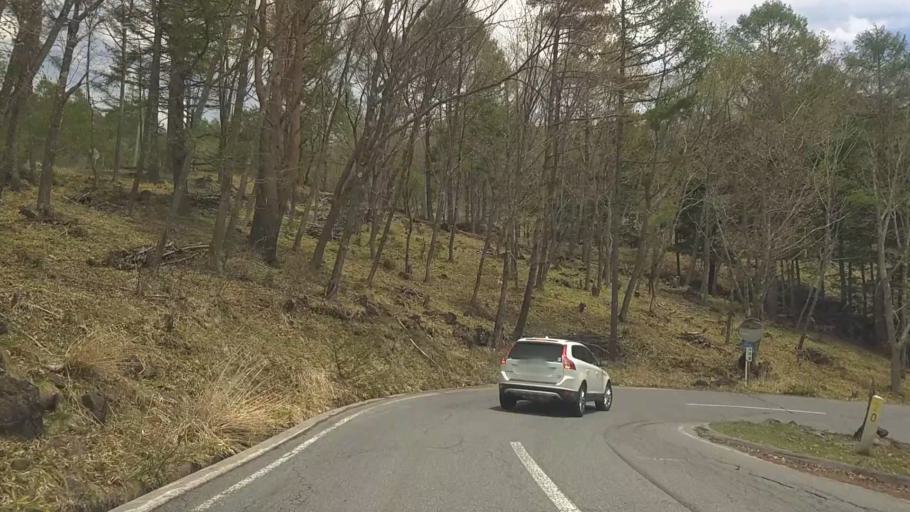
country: JP
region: Nagano
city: Chino
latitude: 36.0466
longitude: 138.3005
